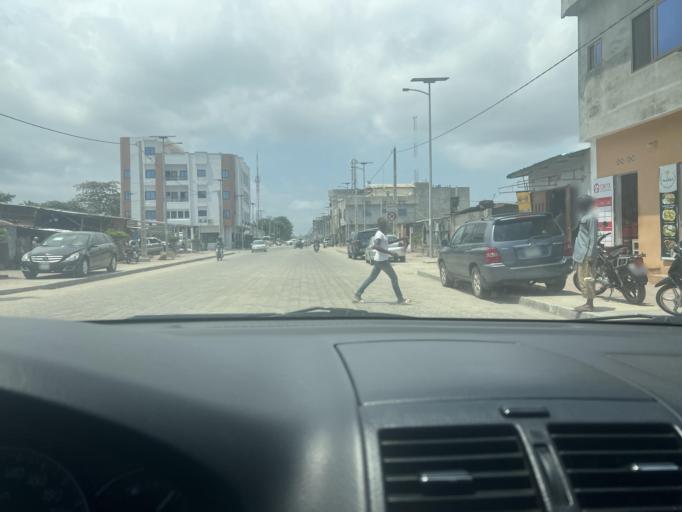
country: BJ
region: Littoral
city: Cotonou
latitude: 6.3804
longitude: 2.4508
